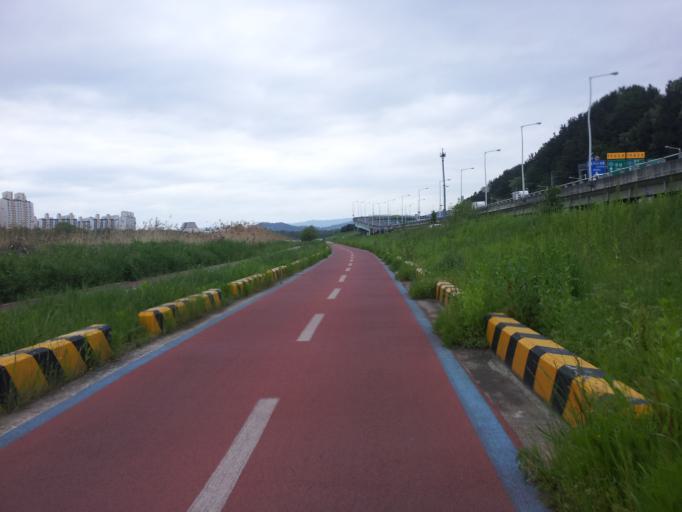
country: KR
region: Daejeon
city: Daejeon
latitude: 36.3599
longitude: 127.4028
